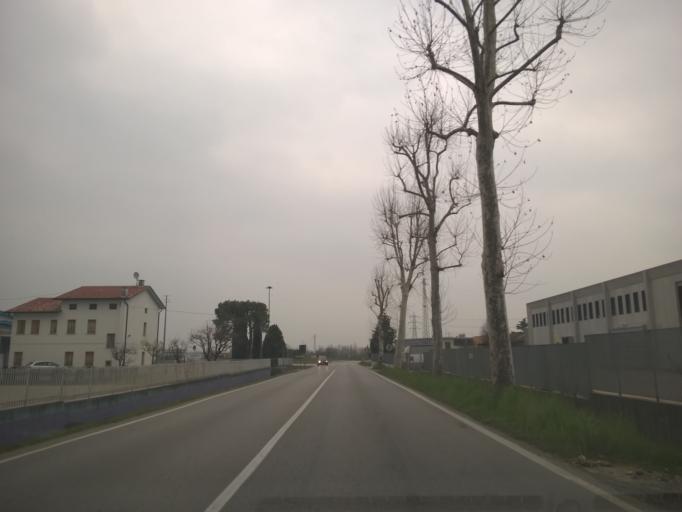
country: IT
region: Veneto
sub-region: Provincia di Vicenza
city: Sandrigo
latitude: 45.6542
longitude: 11.5832
